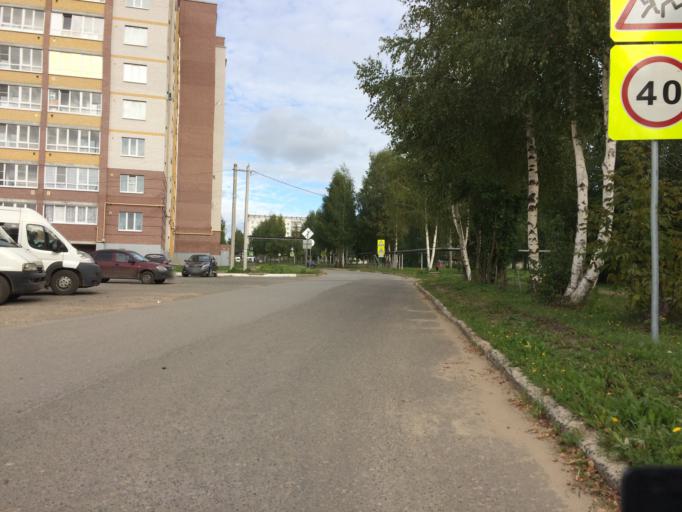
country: RU
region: Mariy-El
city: Yoshkar-Ola
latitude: 56.6505
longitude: 47.9659
